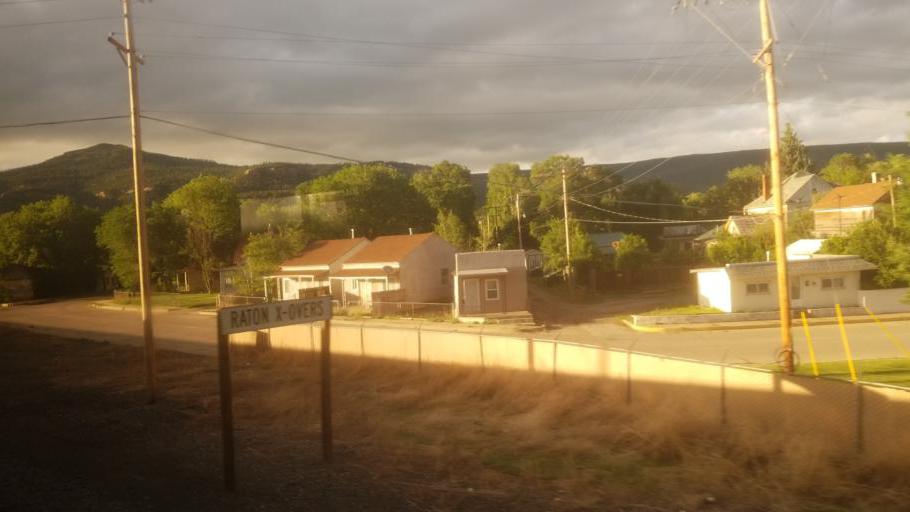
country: US
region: New Mexico
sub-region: Colfax County
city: Raton
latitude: 36.9051
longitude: -104.4386
